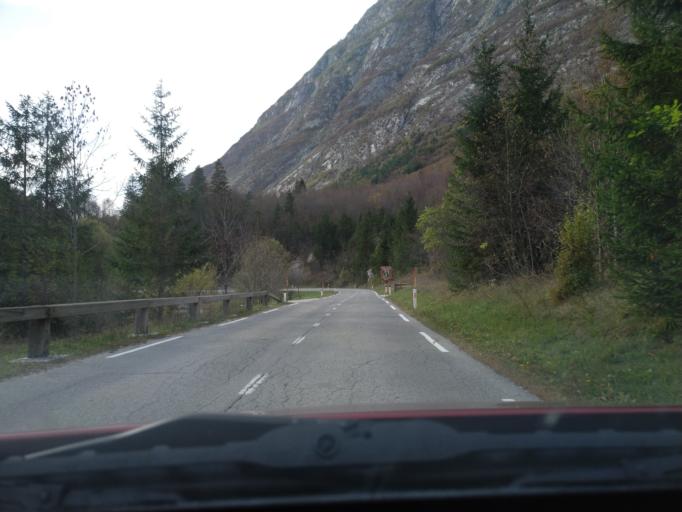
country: SI
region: Bovec
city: Bovec
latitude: 46.3413
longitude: 13.6612
